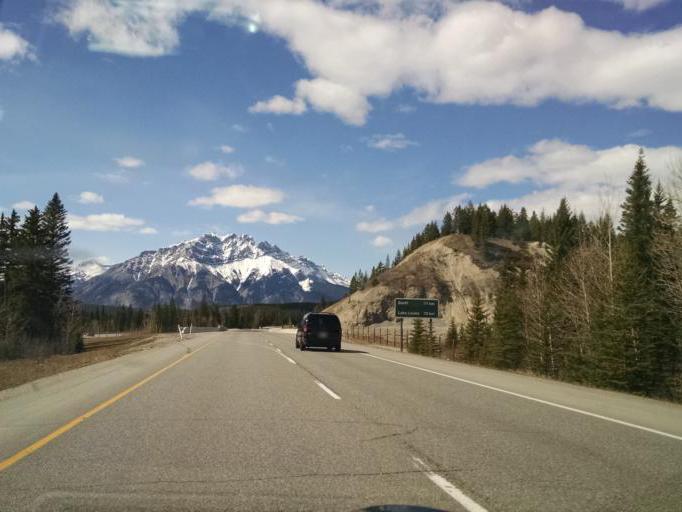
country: CA
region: Alberta
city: Canmore
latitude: 51.1488
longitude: -115.4266
